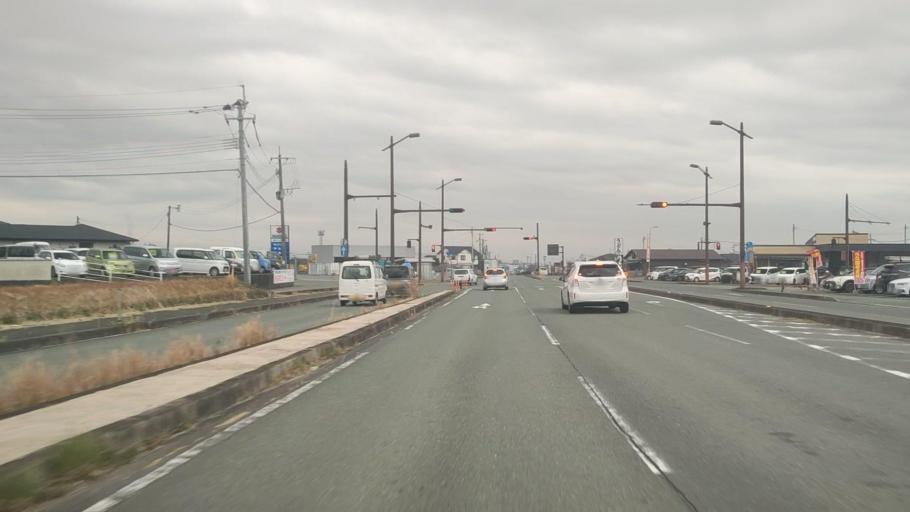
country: JP
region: Kumamoto
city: Ozu
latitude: 32.8341
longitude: 130.8008
